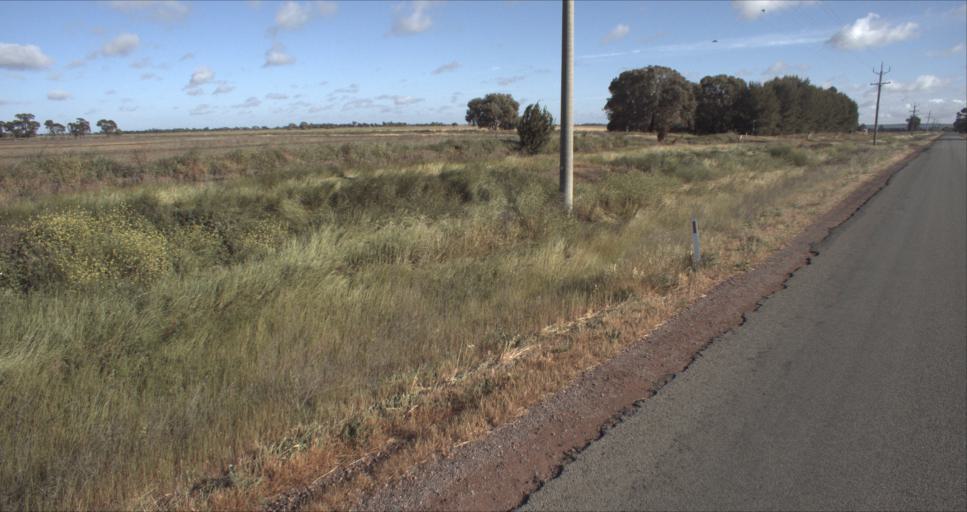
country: AU
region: New South Wales
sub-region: Leeton
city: Leeton
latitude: -34.5249
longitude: 146.3899
